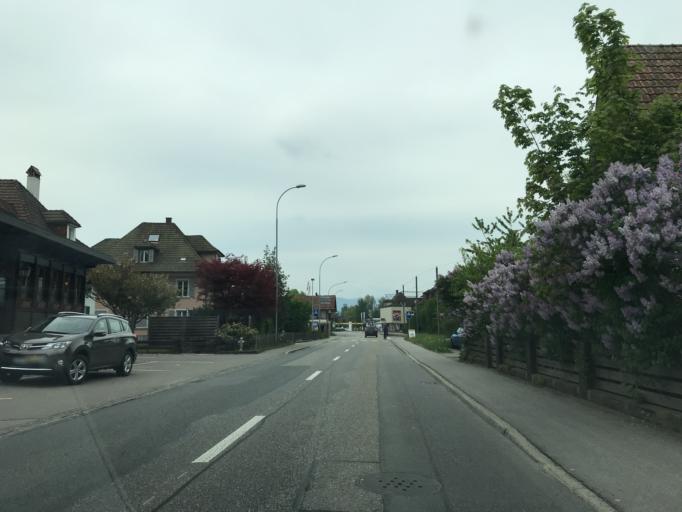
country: CH
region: Bern
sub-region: Oberaargau
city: Aarwangen
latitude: 47.2318
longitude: 7.7755
